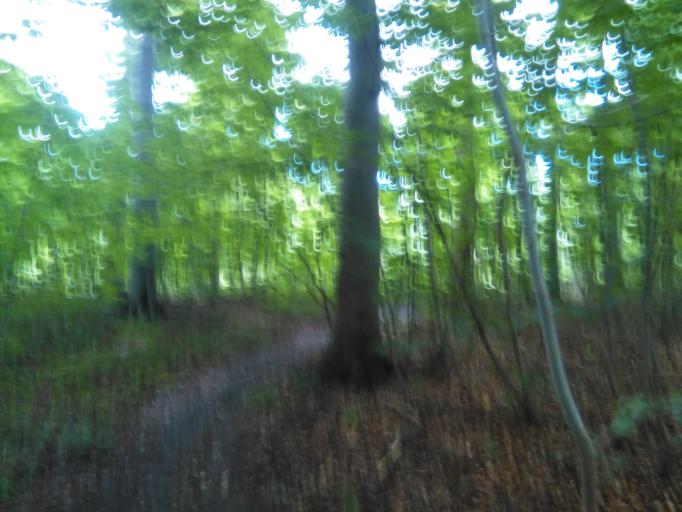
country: DK
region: Central Jutland
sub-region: Arhus Kommune
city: Logten
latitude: 56.2662
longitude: 10.3517
